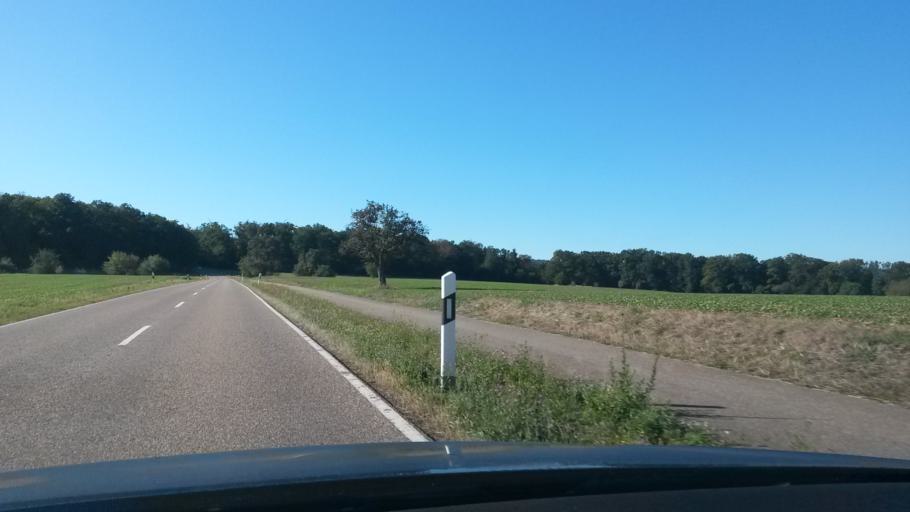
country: DE
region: Baden-Wuerttemberg
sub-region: Karlsruhe Region
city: Neuenburg
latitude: 48.8657
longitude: 8.5353
